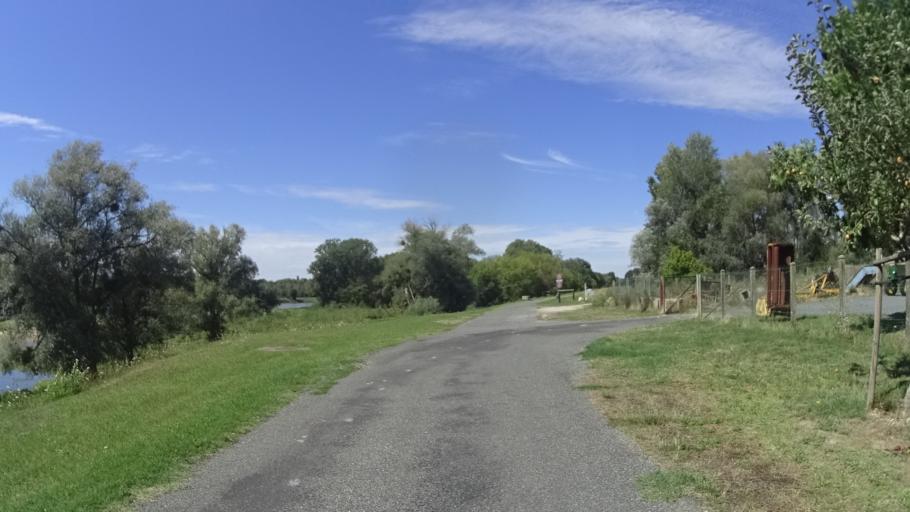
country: FR
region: Centre
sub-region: Departement du Loiret
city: Briare
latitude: 47.5904
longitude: 2.7790
